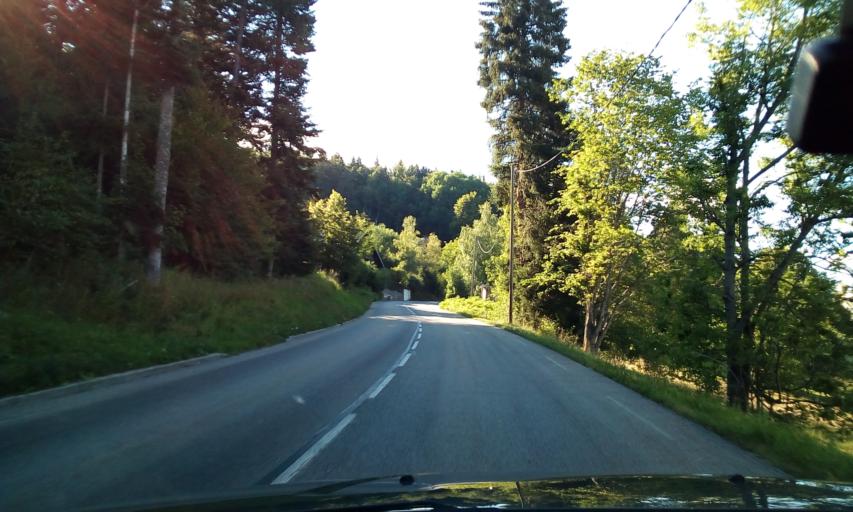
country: FR
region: Rhone-Alpes
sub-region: Departement de l'Isere
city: Seyssins
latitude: 45.1703
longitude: 5.6379
